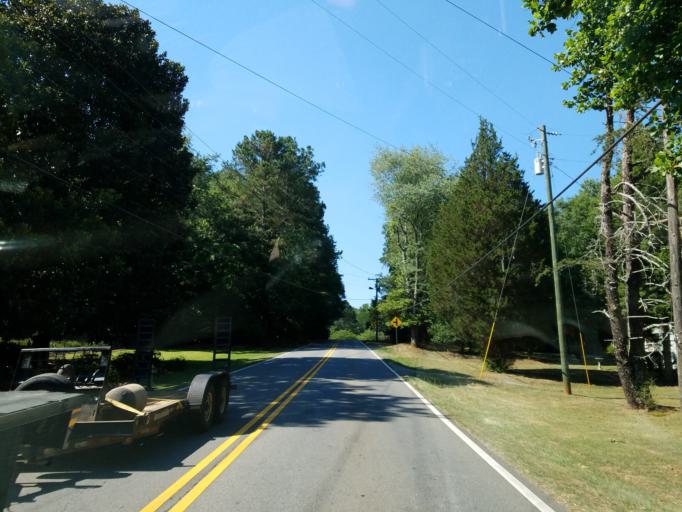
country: US
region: Georgia
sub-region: Fulton County
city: Milton
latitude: 34.1523
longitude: -84.3429
